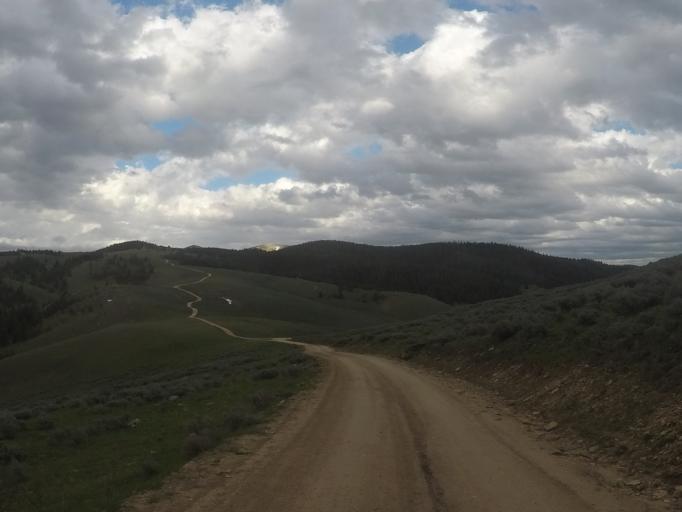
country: US
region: Wyoming
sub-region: Sheridan County
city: Sheridan
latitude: 44.5071
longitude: -107.4573
